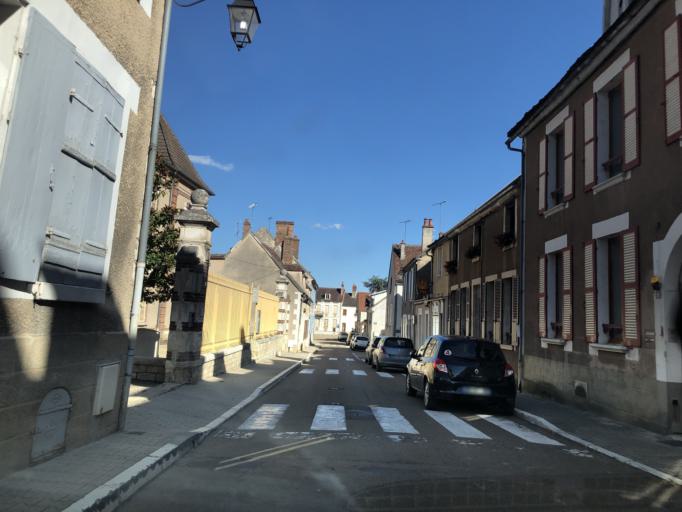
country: FR
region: Bourgogne
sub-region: Departement de l'Yonne
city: Seignelay
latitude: 47.9026
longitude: 3.6023
